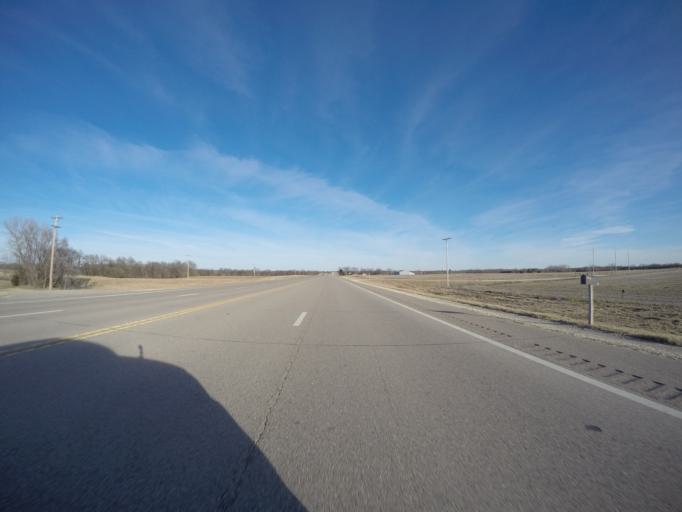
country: US
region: Kansas
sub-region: Marion County
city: Peabody
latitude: 38.1745
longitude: -97.1357
